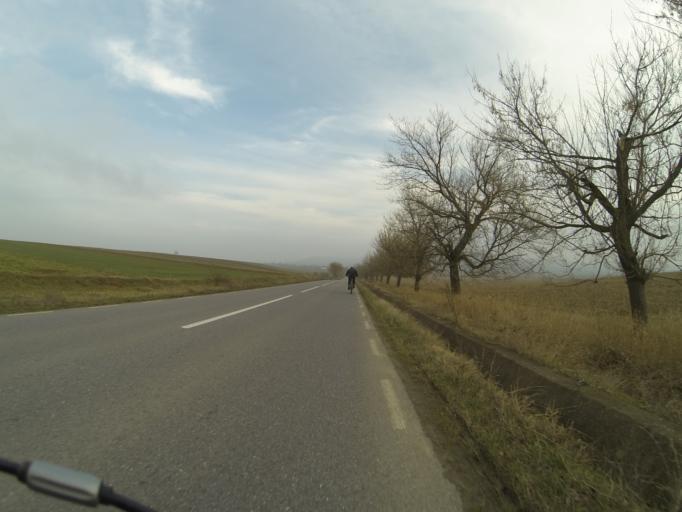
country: RO
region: Mehedinti
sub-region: Comuna Corlatel
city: Corlatel
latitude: 44.4001
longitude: 22.9132
